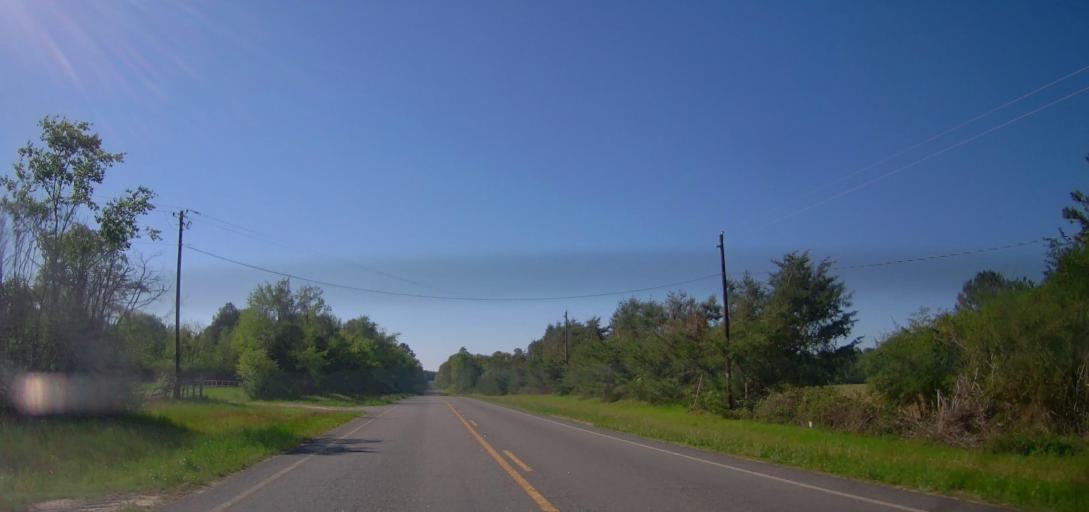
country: US
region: Georgia
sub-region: Wilcox County
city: Rochelle
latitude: 32.0026
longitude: -83.4821
